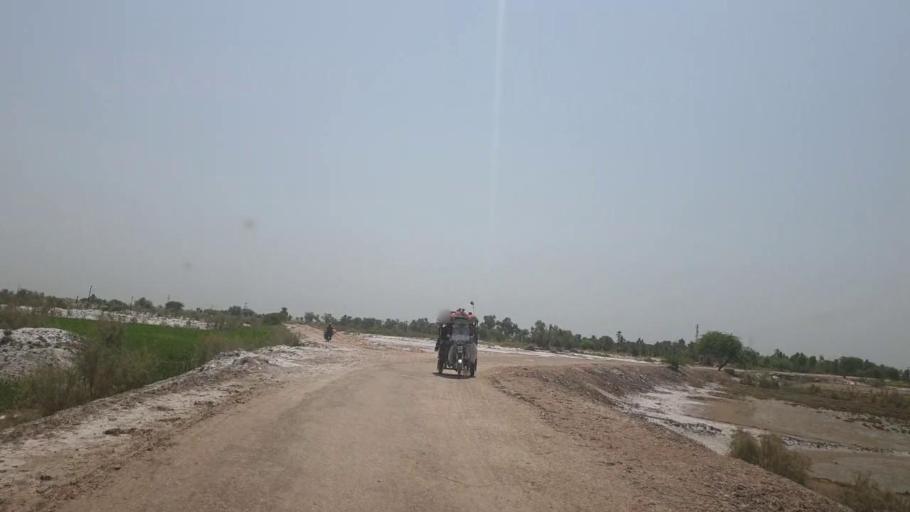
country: PK
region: Sindh
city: Lakhi
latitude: 27.8638
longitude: 68.6629
